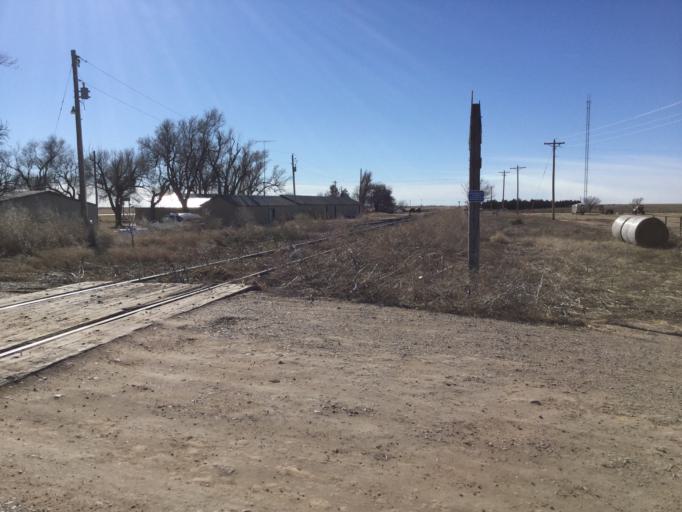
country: US
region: Kansas
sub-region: Morton County
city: Elkhart
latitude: 37.1210
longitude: -101.6369
